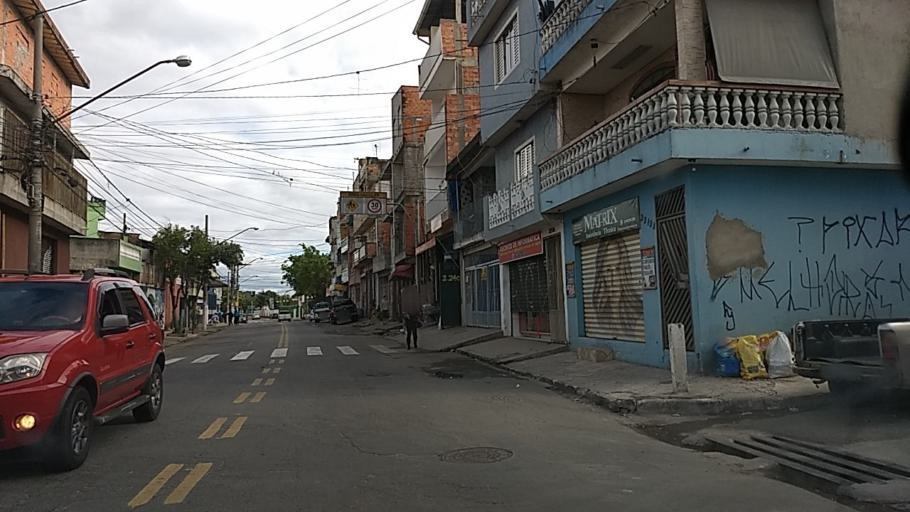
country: BR
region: Sao Paulo
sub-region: Osasco
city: Osasco
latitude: -23.5141
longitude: -46.7833
